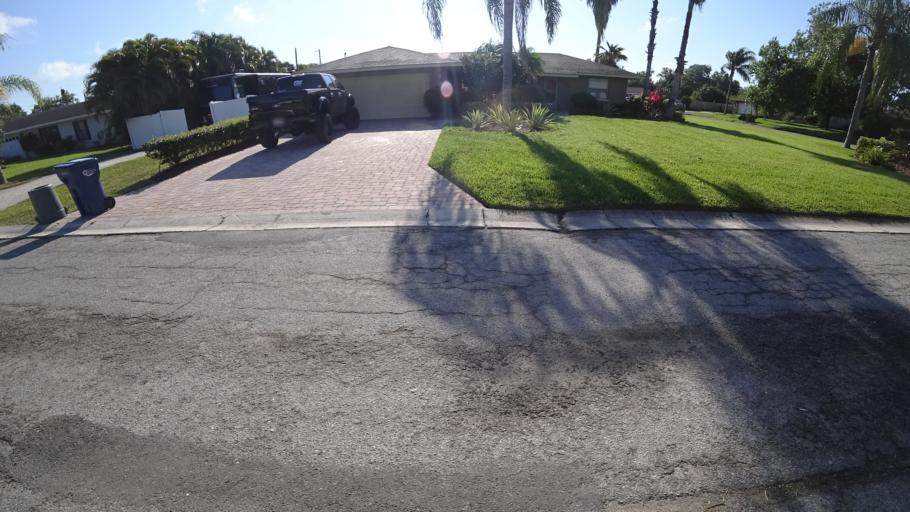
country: US
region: Florida
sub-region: Manatee County
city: Whitfield
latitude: 27.4282
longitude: -82.5586
